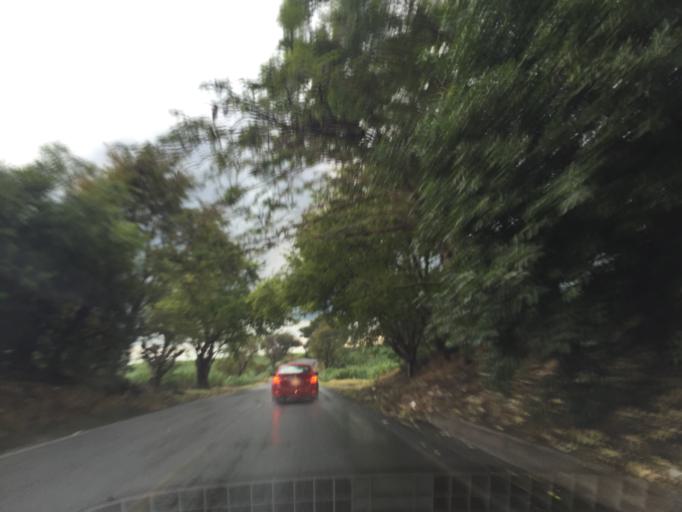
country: MX
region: Colima
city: Queseria
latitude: 19.3801
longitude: -103.5746
